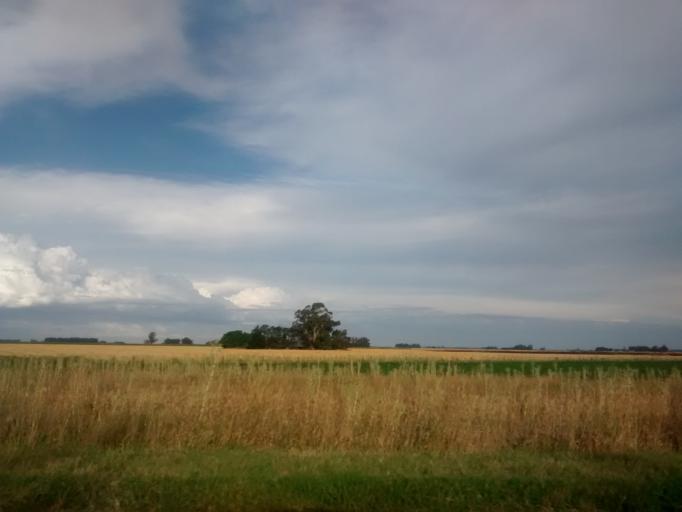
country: AR
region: Buenos Aires
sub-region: Partido de Loberia
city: Loberia
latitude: -38.2174
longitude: -58.7313
